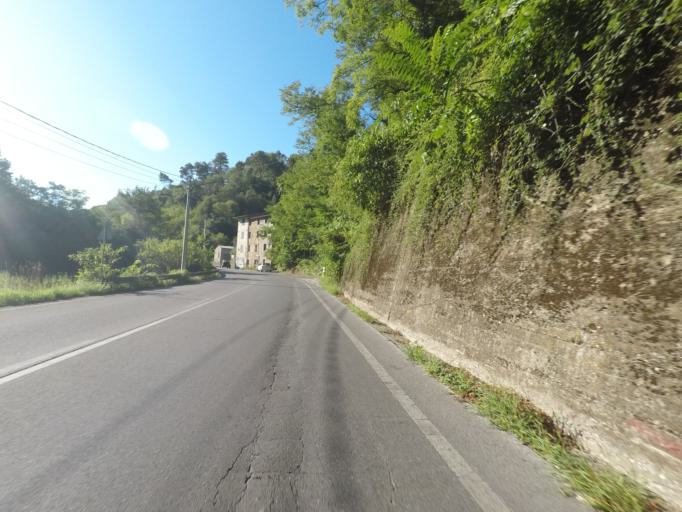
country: IT
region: Tuscany
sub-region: Provincia di Lucca
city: Massarosa
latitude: 43.9031
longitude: 10.3747
